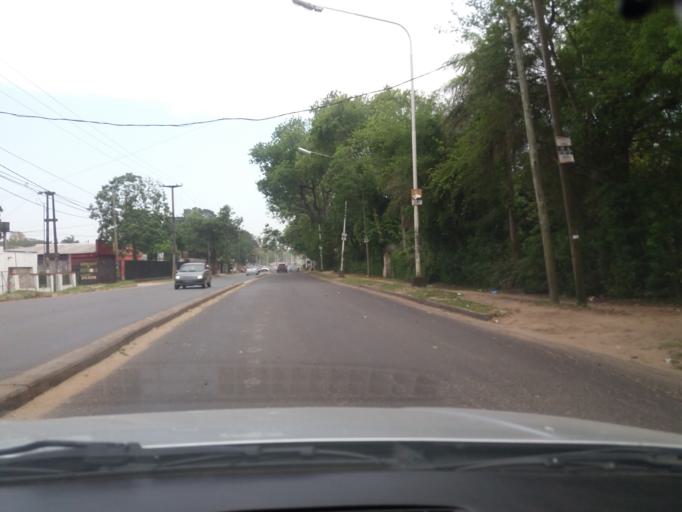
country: AR
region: Corrientes
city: Corrientes
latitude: -27.5093
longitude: -58.8102
